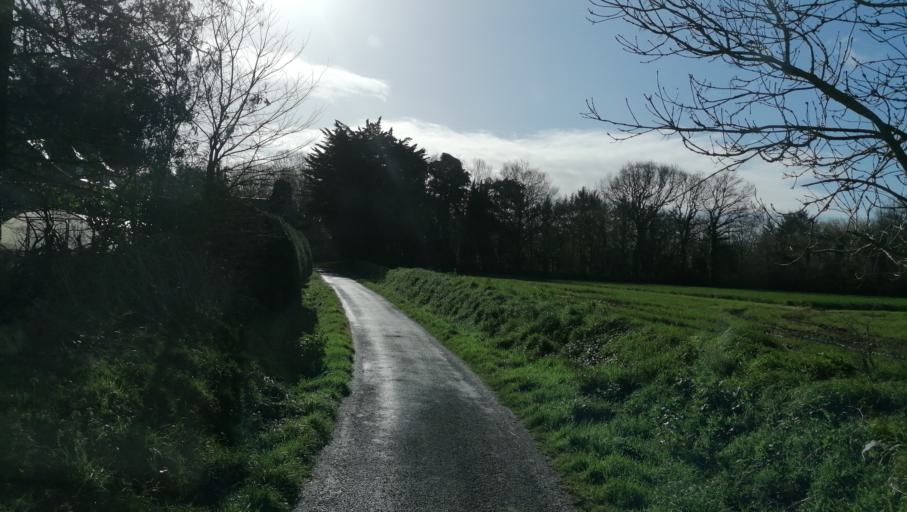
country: FR
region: Brittany
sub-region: Departement des Cotes-d'Armor
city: Pleguien
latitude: 48.6461
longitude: -2.9043
